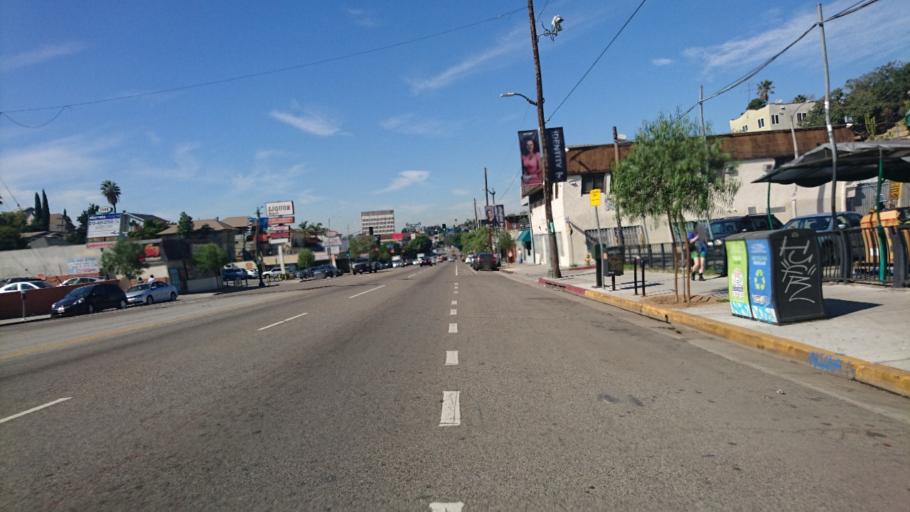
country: US
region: California
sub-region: Los Angeles County
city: Echo Park
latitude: 34.0758
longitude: -118.2548
